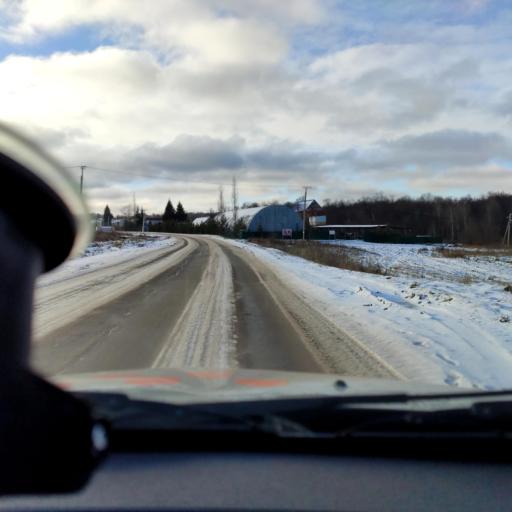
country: RU
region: Bashkortostan
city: Mikhaylovka
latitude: 54.7906
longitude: 55.7635
